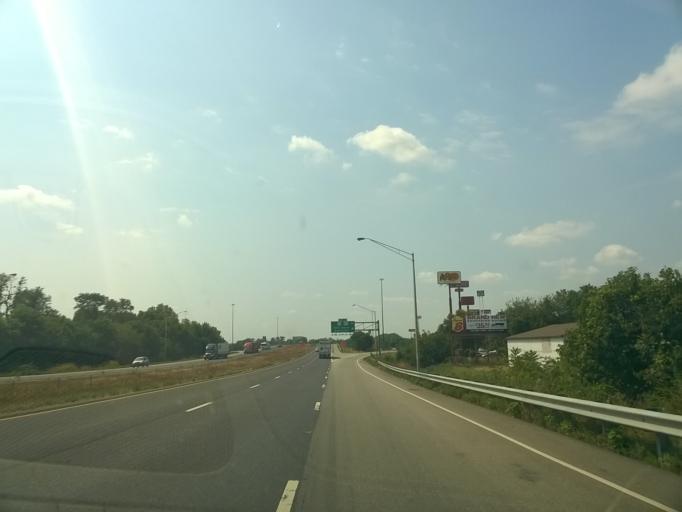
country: US
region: Indiana
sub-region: Vigo County
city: Terre Haute
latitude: 39.4311
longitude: -87.4108
